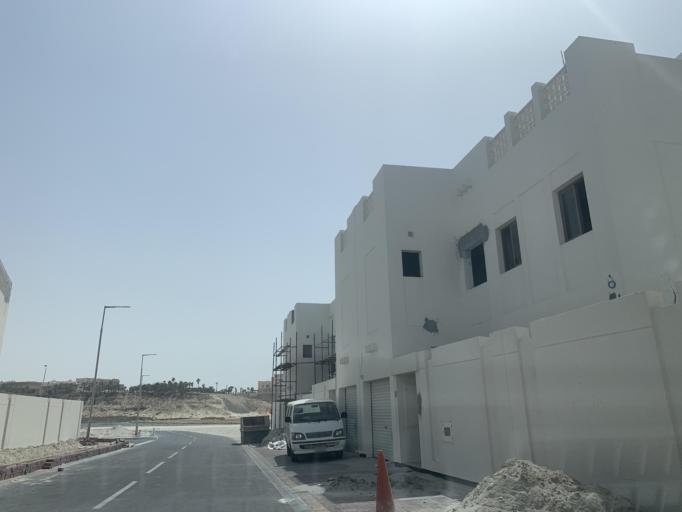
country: BH
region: Northern
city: Ar Rifa'
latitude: 26.1490
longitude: 50.5652
